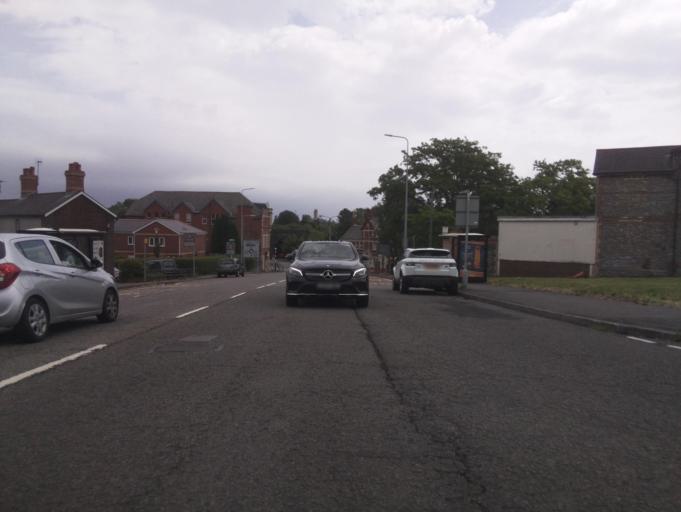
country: GB
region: Wales
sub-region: Vale of Glamorgan
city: Barry
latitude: 51.4110
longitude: -3.2537
